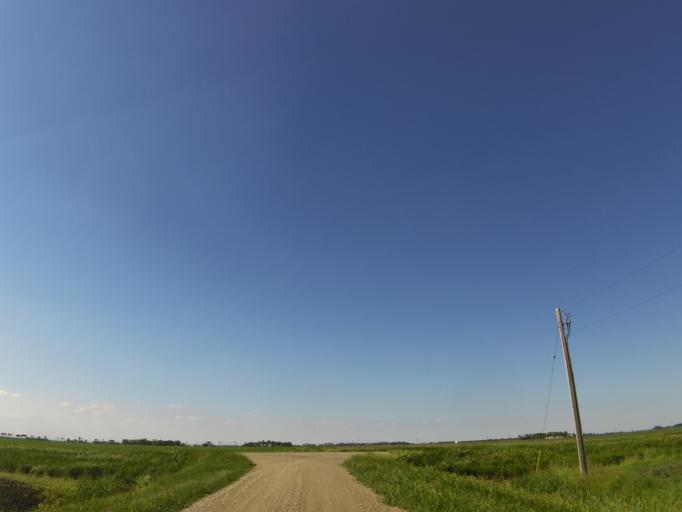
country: US
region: North Dakota
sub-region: Walsh County
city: Grafton
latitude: 48.3530
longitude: -97.2330
